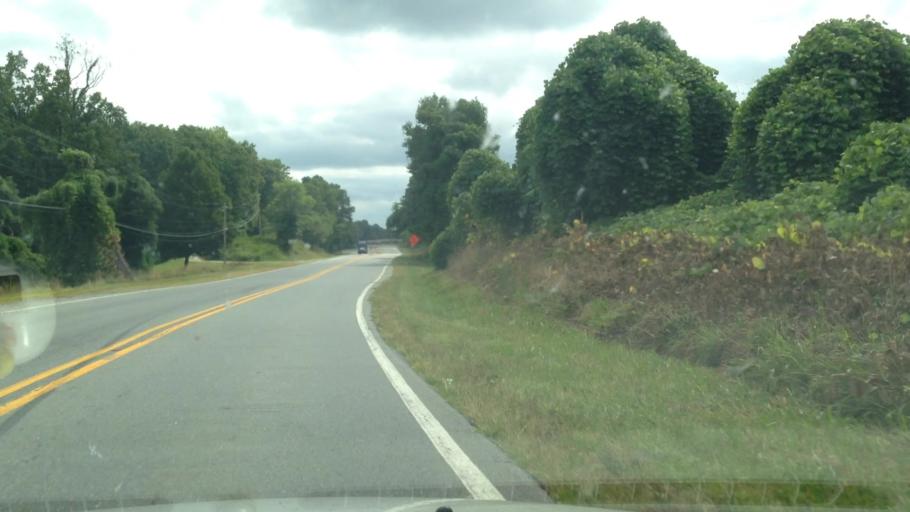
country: US
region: North Carolina
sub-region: Rockingham County
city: Reidsville
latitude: 36.4329
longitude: -79.5781
